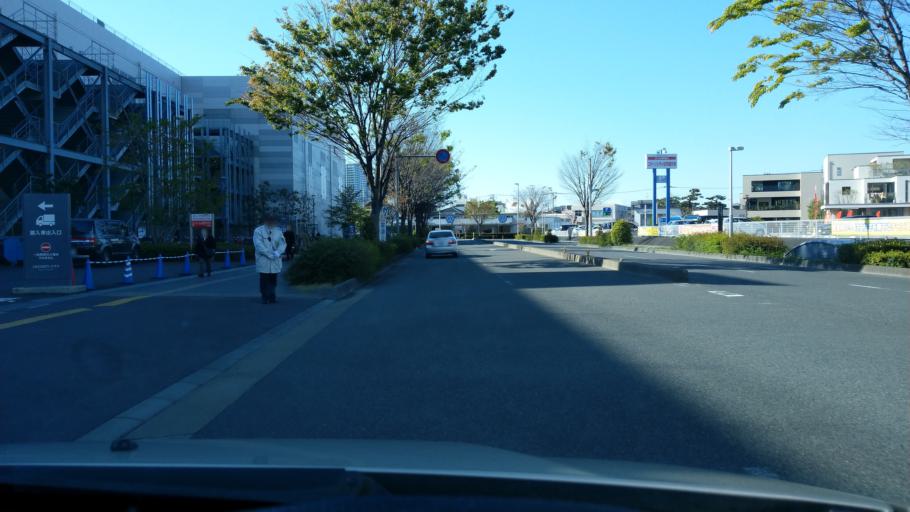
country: JP
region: Saitama
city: Yono
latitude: 35.8967
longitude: 139.6363
